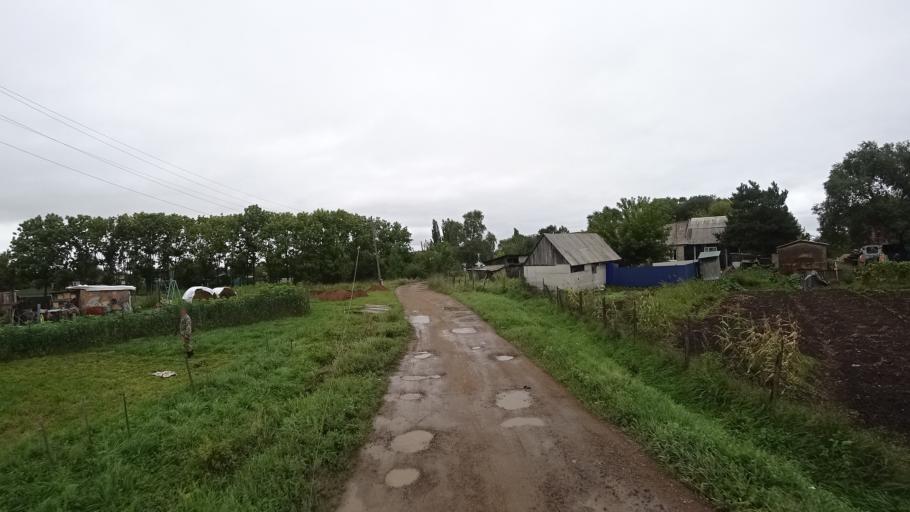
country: RU
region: Primorskiy
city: Chernigovka
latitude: 44.3379
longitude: 132.5440
